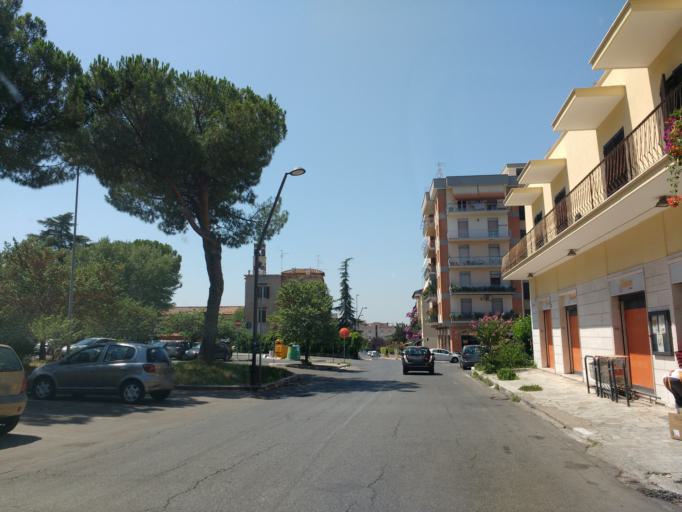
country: IT
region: Latium
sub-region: Citta metropolitana di Roma Capitale
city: Villa Adriana
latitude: 41.9521
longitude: 12.7766
